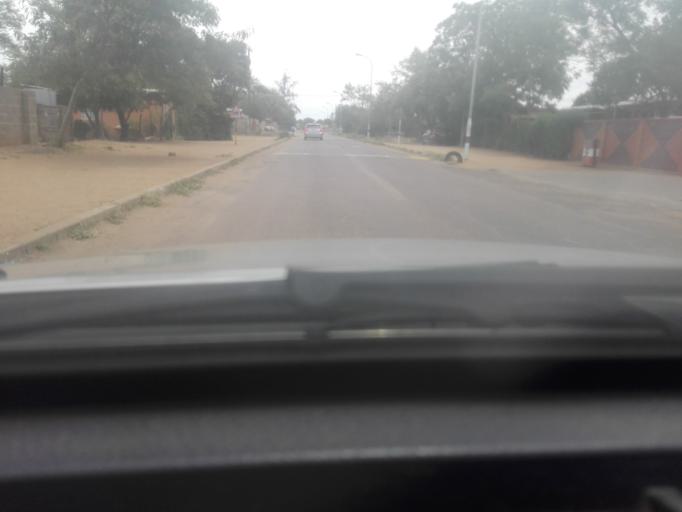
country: BW
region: South East
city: Gaborone
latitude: -24.6222
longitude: 25.9396
